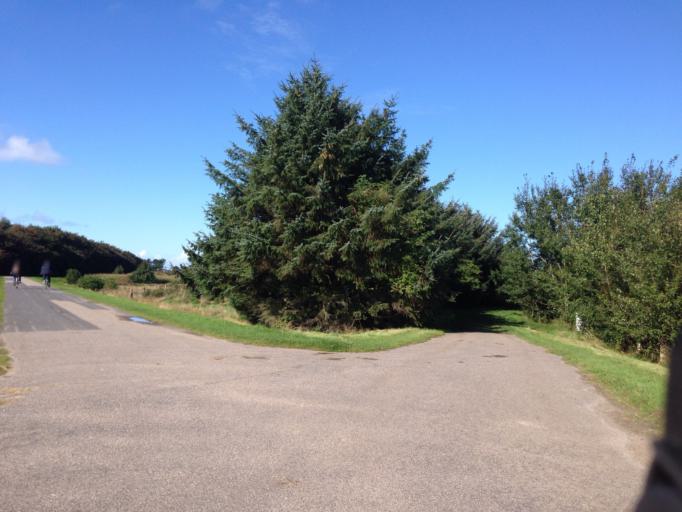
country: DE
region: Schleswig-Holstein
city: Nieblum
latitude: 54.6834
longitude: 8.4810
